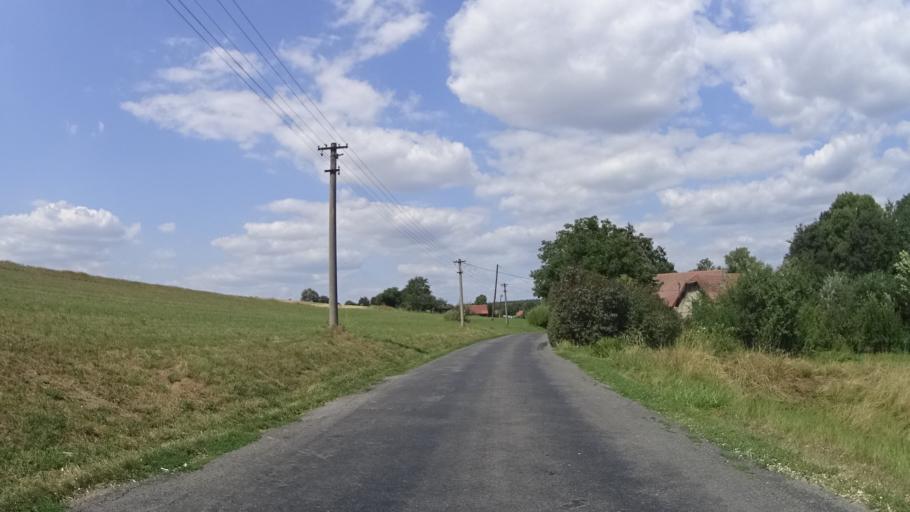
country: CZ
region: Kralovehradecky
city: Kopidlno
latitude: 50.3955
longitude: 15.2853
